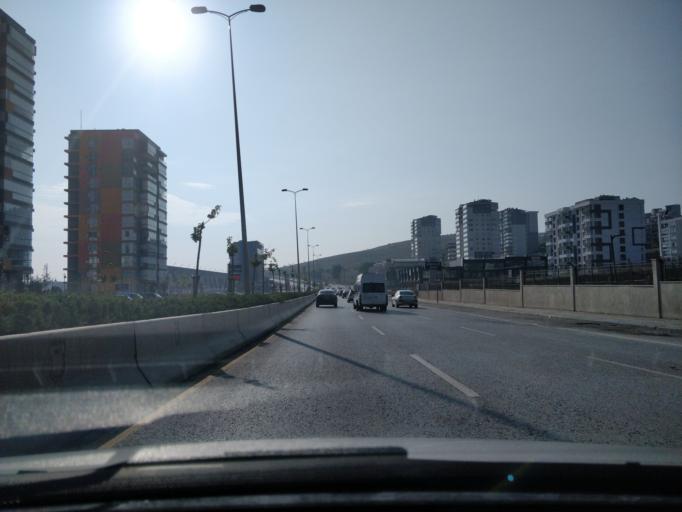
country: TR
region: Ankara
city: Etimesgut
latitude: 39.8968
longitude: 32.6544
